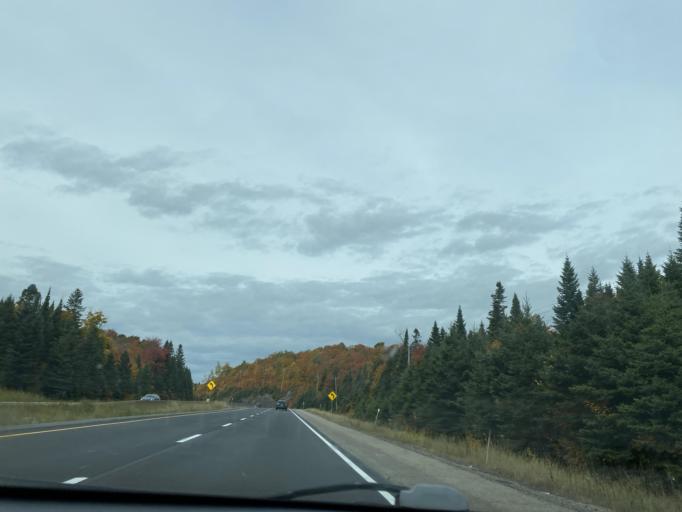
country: CA
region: Quebec
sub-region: Laurentides
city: Sainte-Agathe-des-Monts
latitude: 46.0861
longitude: -74.3240
